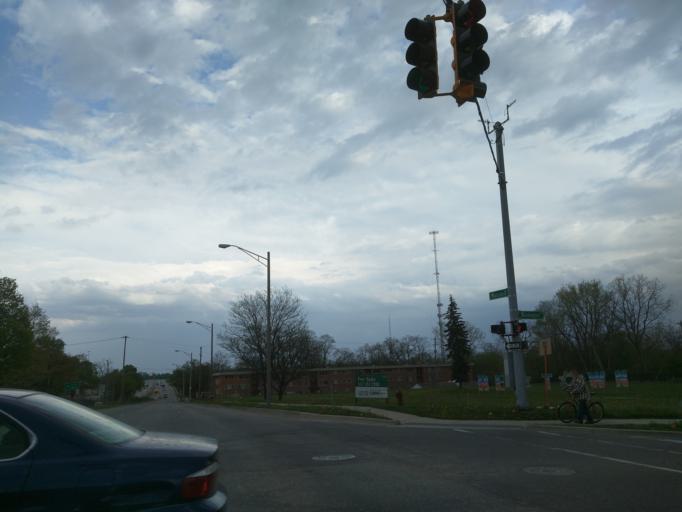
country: US
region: Michigan
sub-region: Ingham County
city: Lansing
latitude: 42.7255
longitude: -84.5523
